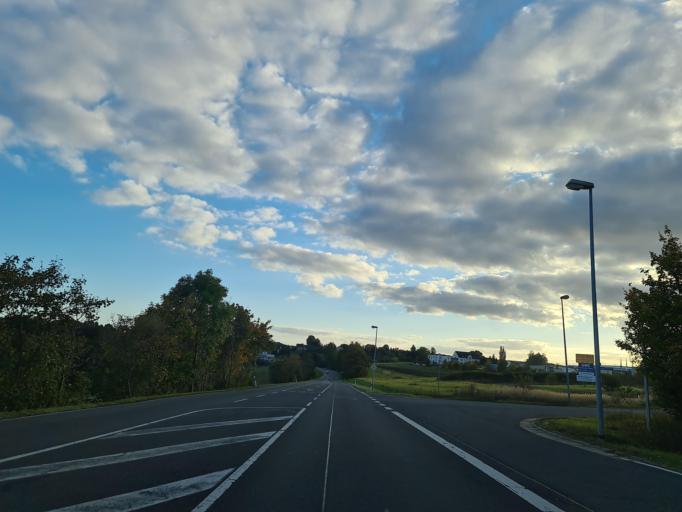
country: DE
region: Thuringia
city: Teichwitz
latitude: 50.7449
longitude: 12.0877
